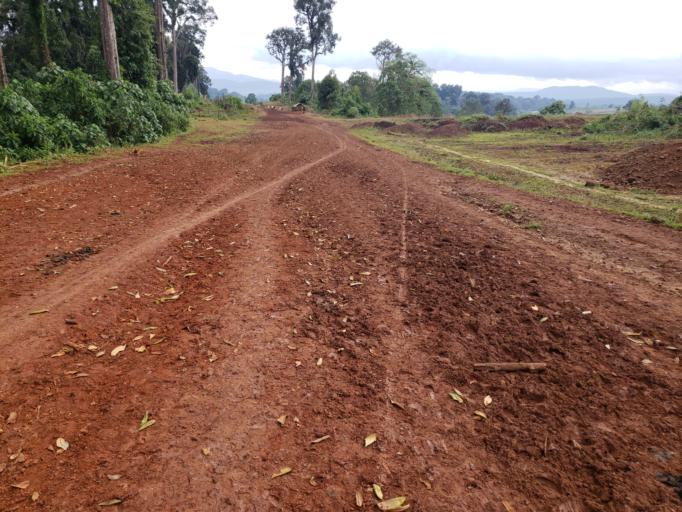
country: ET
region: Oromiya
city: Dodola
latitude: 6.5530
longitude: 39.4227
